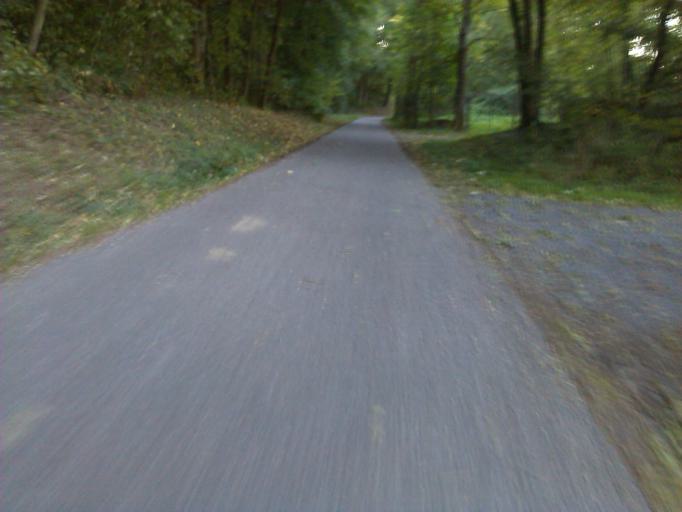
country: DE
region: Baden-Wuerttemberg
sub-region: Regierungsbezirk Stuttgart
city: Ittlingen
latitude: 49.2100
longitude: 8.9245
